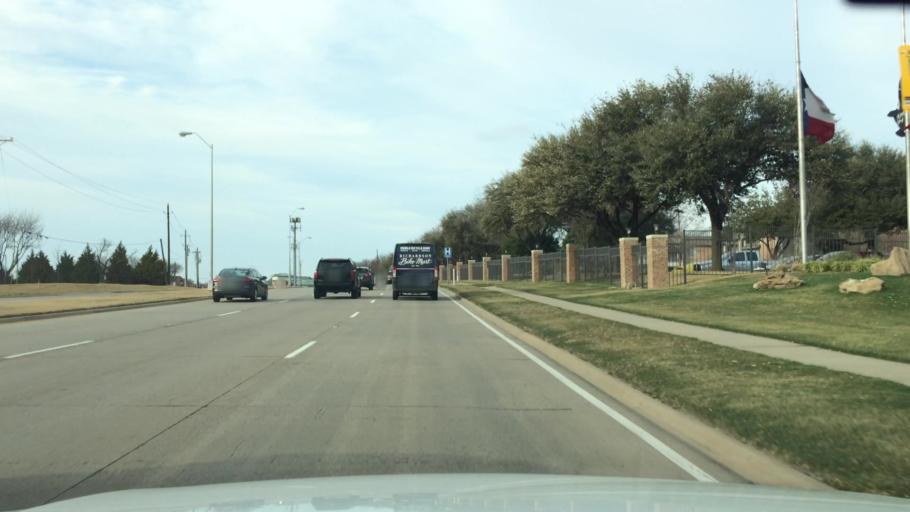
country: US
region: Texas
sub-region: Collin County
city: Frisco
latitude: 33.0752
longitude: -96.7959
